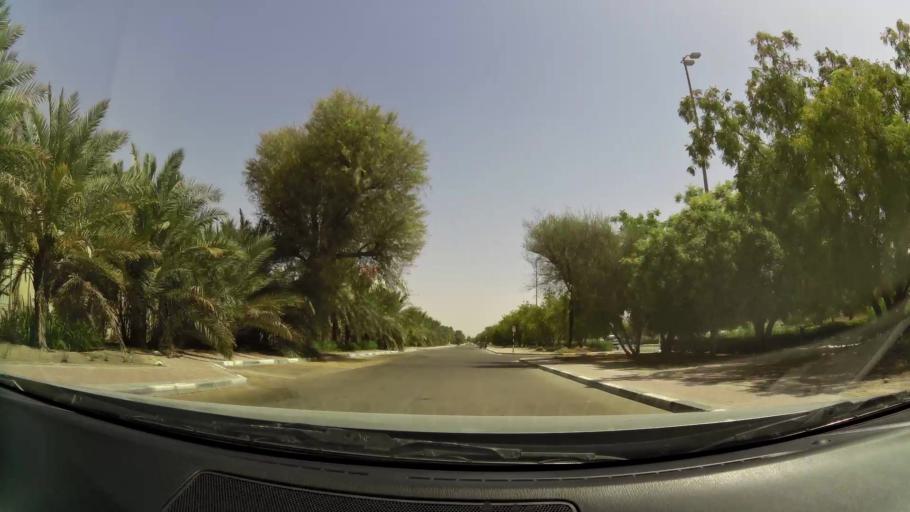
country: OM
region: Al Buraimi
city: Al Buraymi
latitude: 24.2823
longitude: 55.7824
